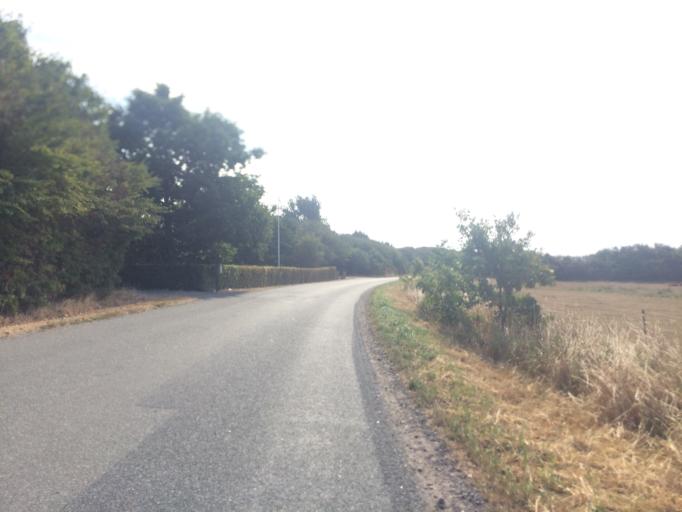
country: DK
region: North Denmark
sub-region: Morso Kommune
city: Nykobing Mors
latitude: 56.6516
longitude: 8.7813
